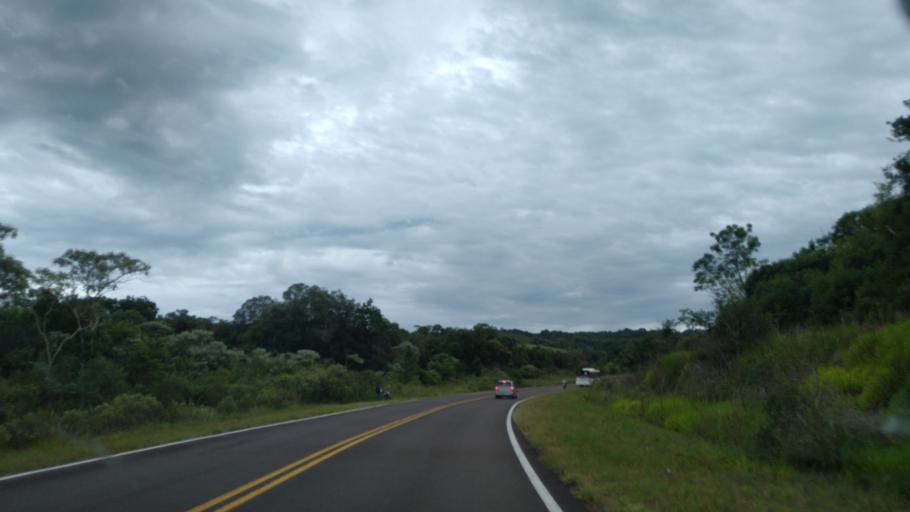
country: AR
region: Misiones
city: Bernardo de Irigoyen
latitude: -26.3212
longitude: -53.7531
